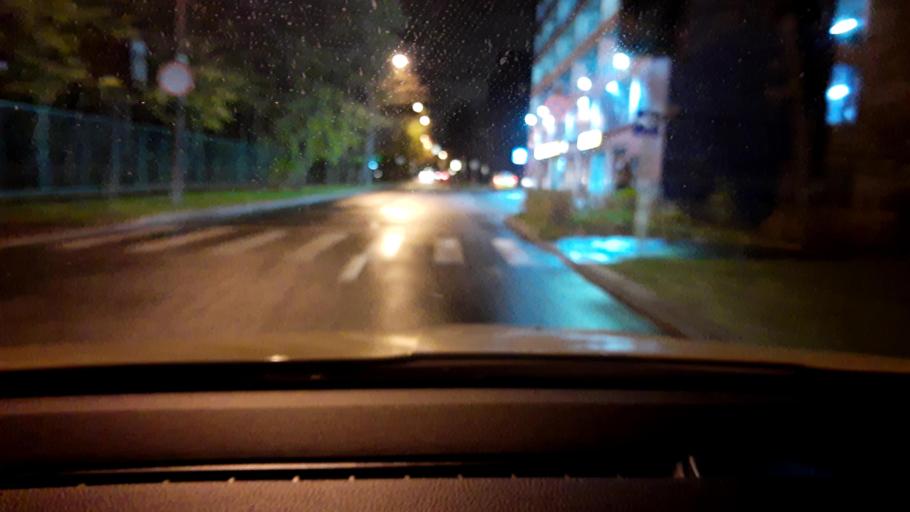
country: RU
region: Moscow
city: Vatutino
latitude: 55.8820
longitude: 37.6959
